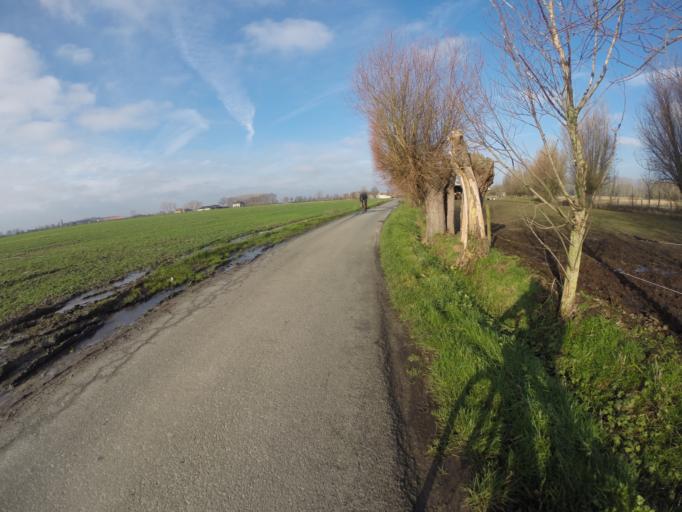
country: BE
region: Flanders
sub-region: Provincie Oost-Vlaanderen
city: Nevele
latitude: 51.0522
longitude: 3.5038
